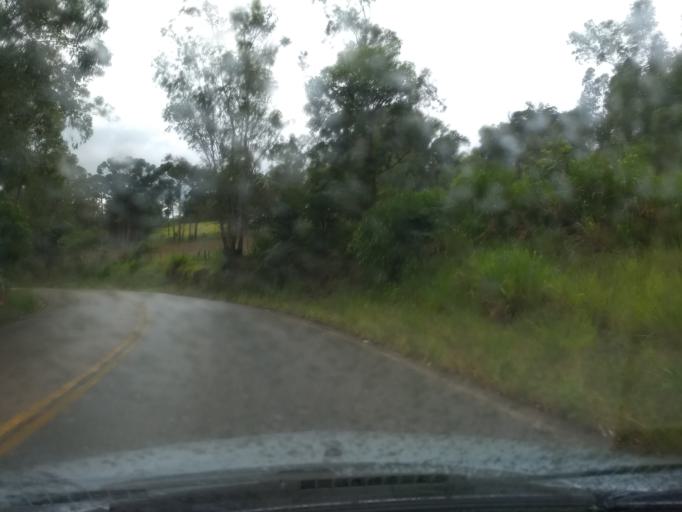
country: BR
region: Minas Gerais
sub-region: Extrema
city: Extrema
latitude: -22.7678
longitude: -46.3257
